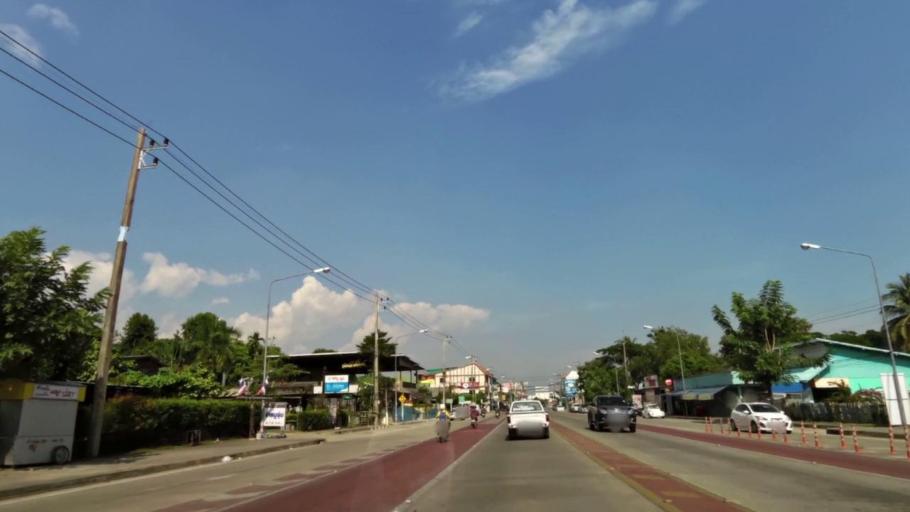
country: TH
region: Chiang Rai
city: Chiang Rai
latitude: 19.9209
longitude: 99.8335
